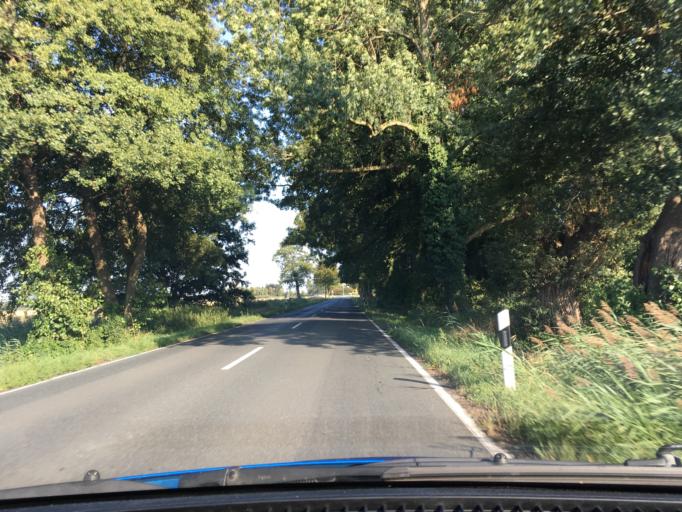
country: DE
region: Lower Saxony
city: Isernhagen Farster Bauerschaft
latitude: 52.4879
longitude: 9.8680
